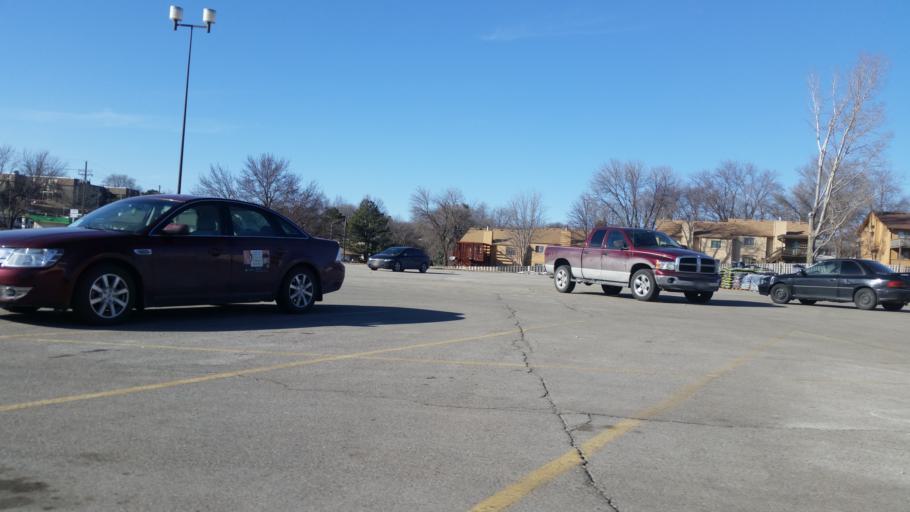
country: US
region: Nebraska
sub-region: Sarpy County
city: Bellevue
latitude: 41.1544
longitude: -95.9177
